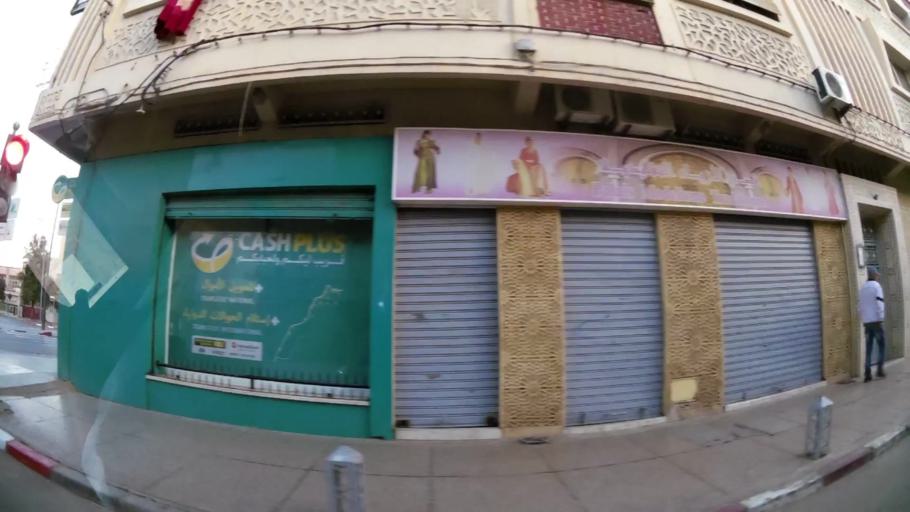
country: MA
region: Oriental
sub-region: Oujda-Angad
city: Oujda
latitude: 34.6974
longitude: -1.9193
